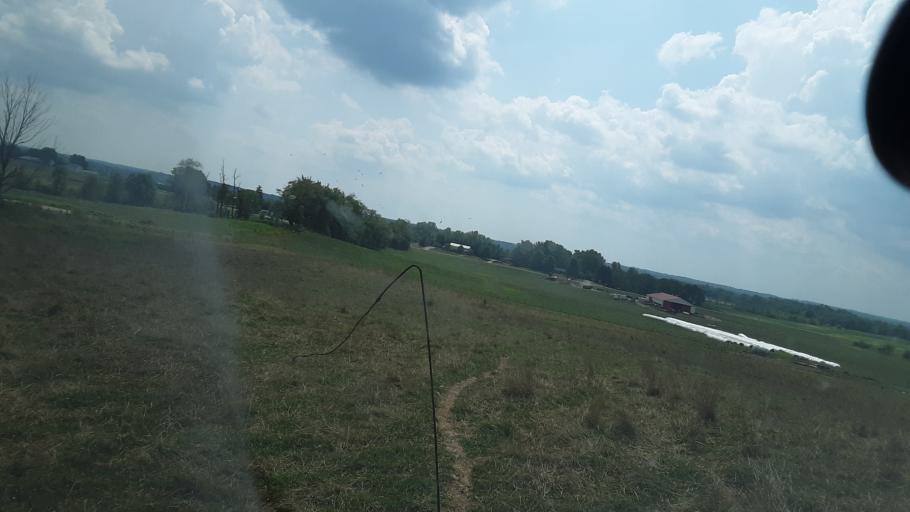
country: US
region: Ohio
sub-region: Knox County
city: Fredericktown
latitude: 40.4788
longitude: -82.6636
